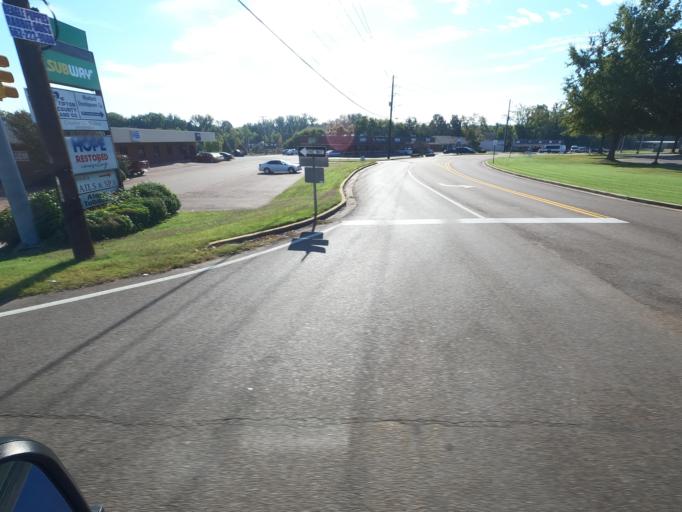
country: US
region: Tennessee
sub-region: Tipton County
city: Atoka
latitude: 35.4495
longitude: -89.7817
